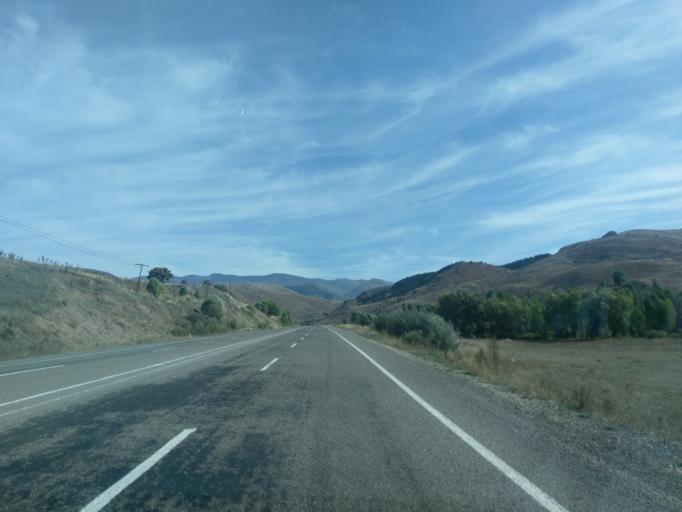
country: TR
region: Sivas
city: Imranli
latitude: 39.8435
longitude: 38.2870
